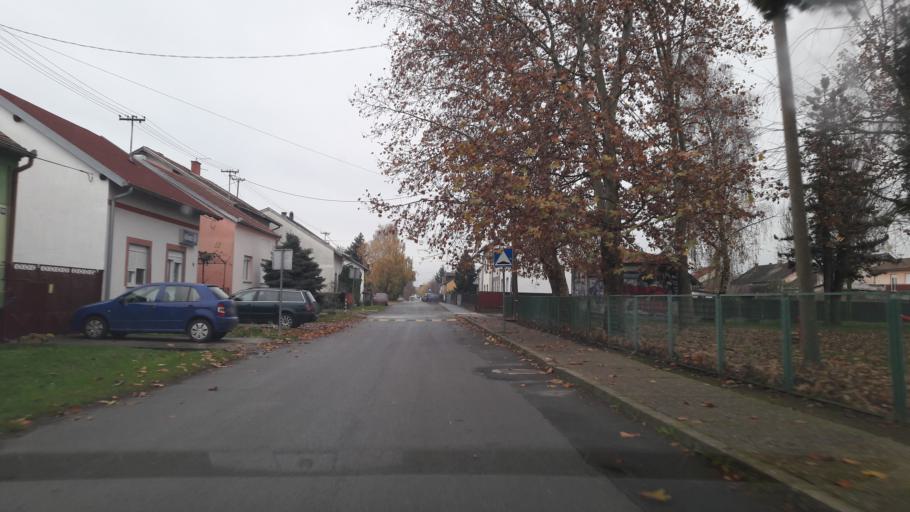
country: HR
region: Osjecko-Baranjska
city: Visnjevac
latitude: 45.5655
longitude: 18.6126
